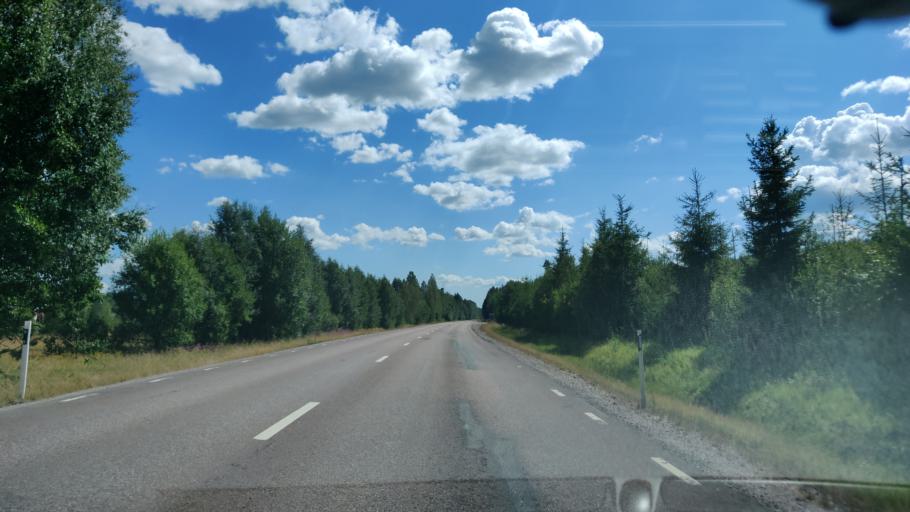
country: SE
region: Vaermland
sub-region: Hagfors Kommun
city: Ekshaerad
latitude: 60.2046
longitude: 13.4914
